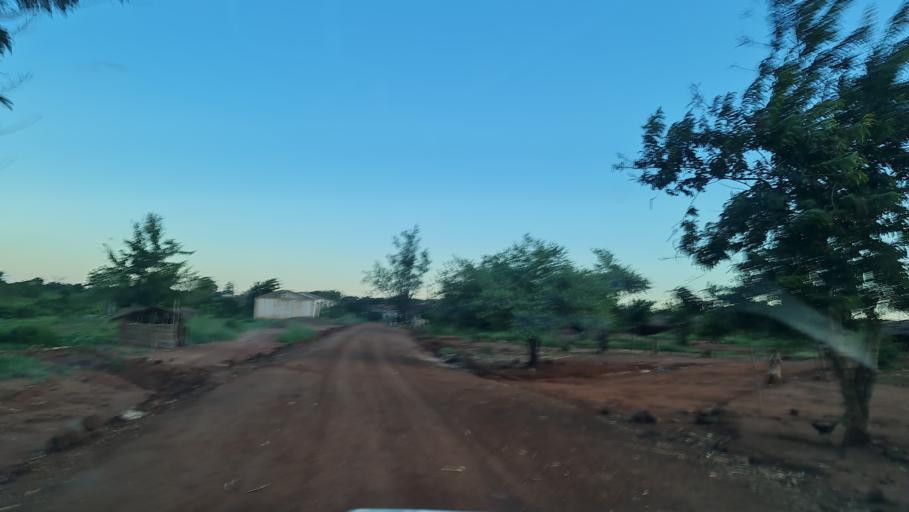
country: MZ
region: Nampula
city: Ilha de Mocambique
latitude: -14.9830
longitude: 40.0944
